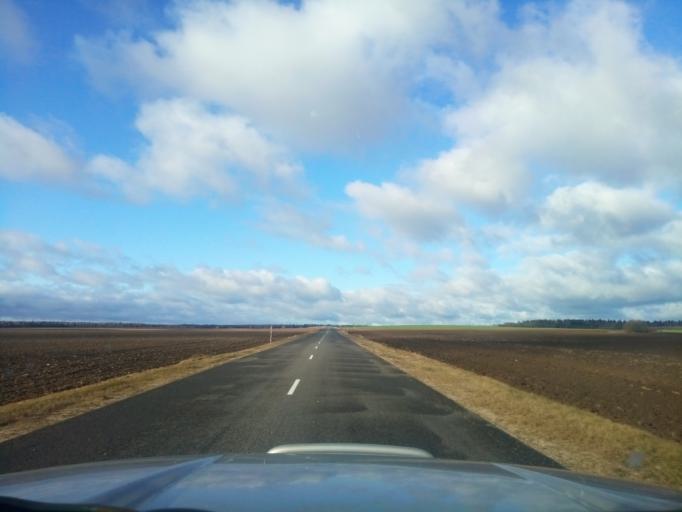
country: BY
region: Minsk
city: Kapyl'
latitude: 53.1651
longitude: 27.0627
